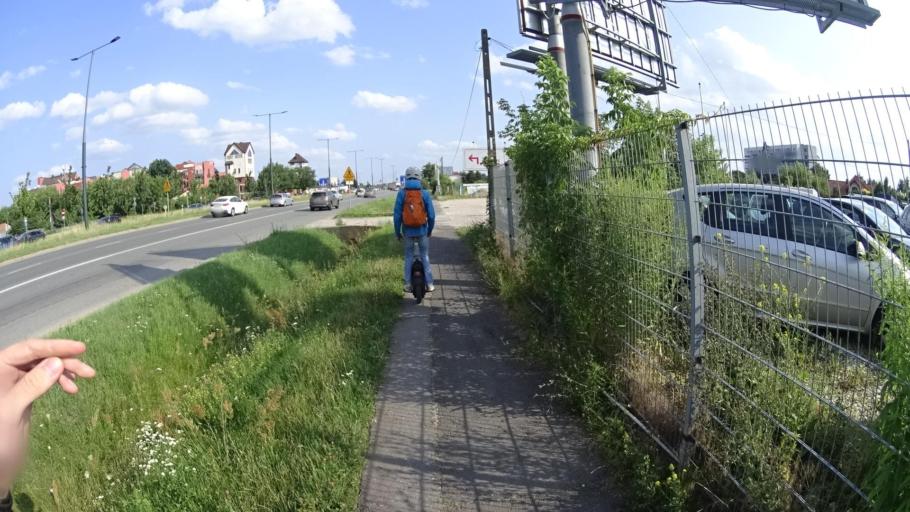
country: PL
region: Masovian Voivodeship
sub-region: Warszawa
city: Bialoleka
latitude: 52.3460
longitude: 20.9513
